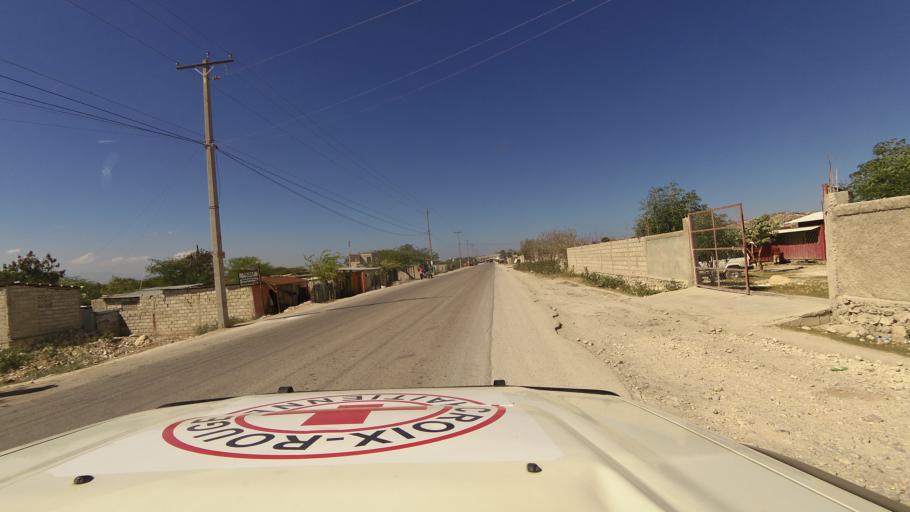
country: HT
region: Ouest
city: Croix des Bouquets
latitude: 18.6487
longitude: -72.2537
